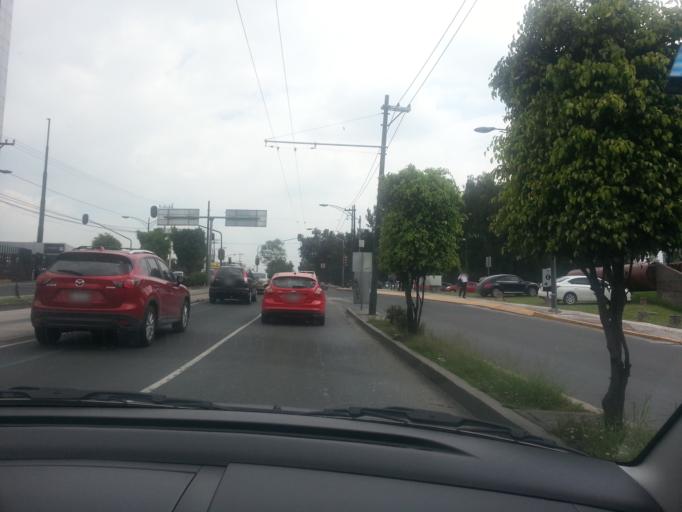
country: MX
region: Mexico City
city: Magdalena Contreras
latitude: 19.3380
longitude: -99.1903
